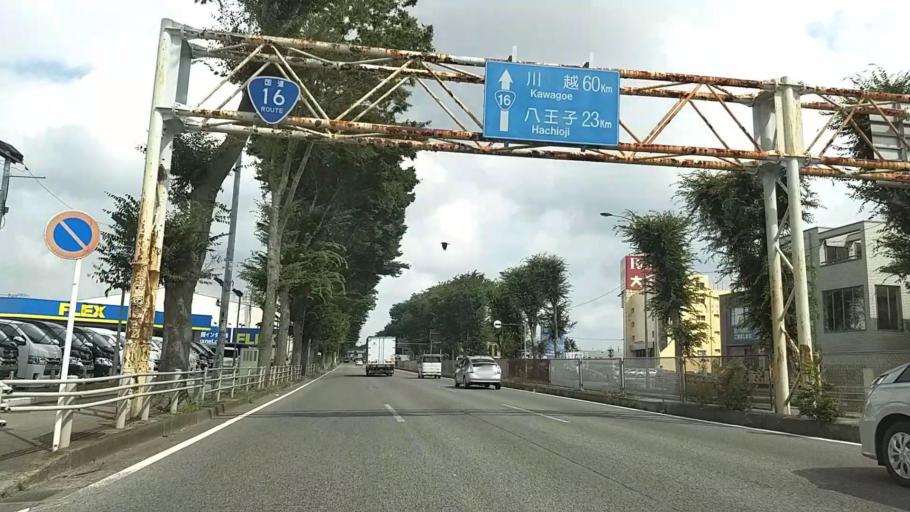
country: JP
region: Tokyo
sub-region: Machida-shi
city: Machida
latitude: 35.5188
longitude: 139.4535
